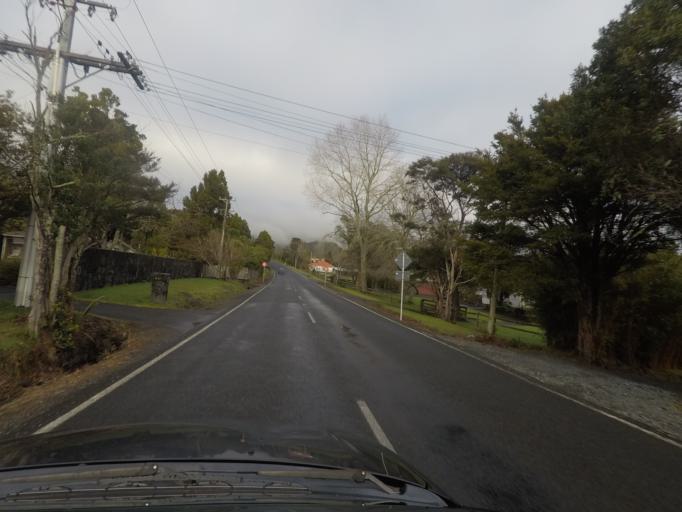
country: NZ
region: Auckland
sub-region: Auckland
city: Waitakere
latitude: -36.9176
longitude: 174.5890
